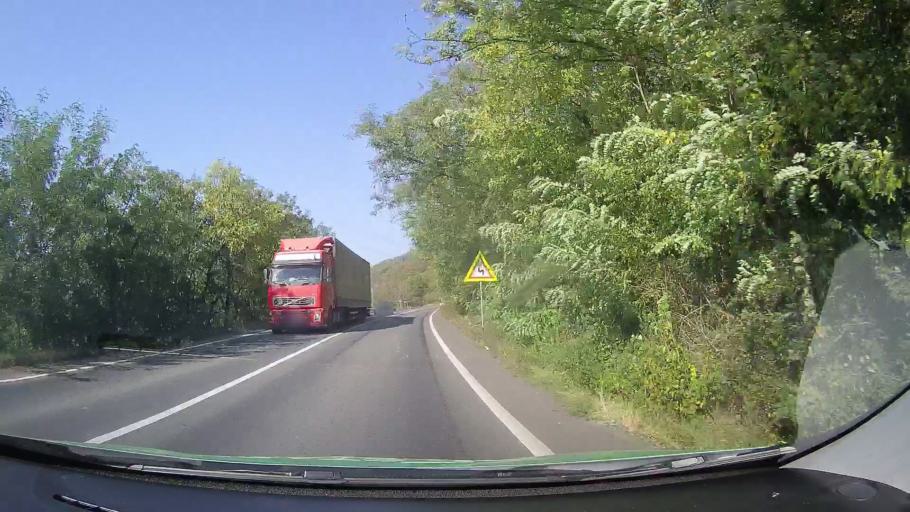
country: RO
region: Arad
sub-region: Comuna Savarsin
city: Savarsin
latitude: 45.9970
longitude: 22.2921
